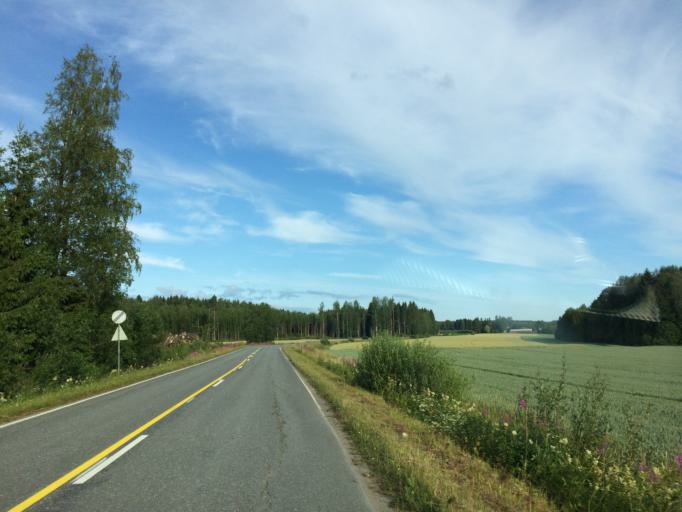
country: FI
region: Haeme
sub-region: Haemeenlinna
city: Janakkala
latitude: 60.9308
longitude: 24.5511
